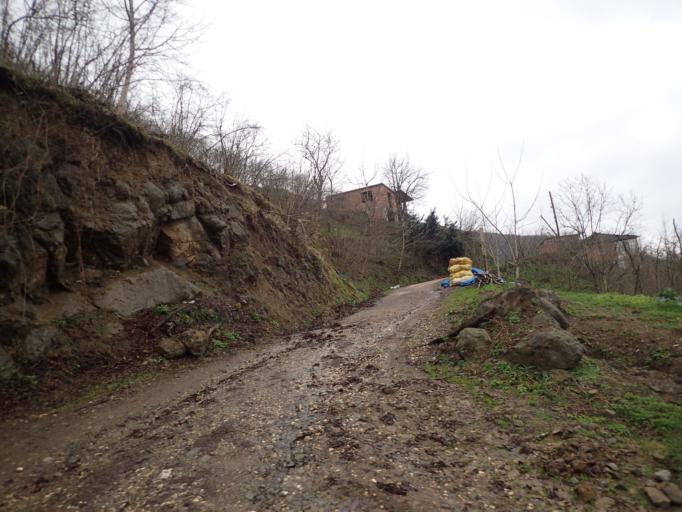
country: TR
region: Ordu
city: Camas
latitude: 40.8717
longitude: 37.5072
